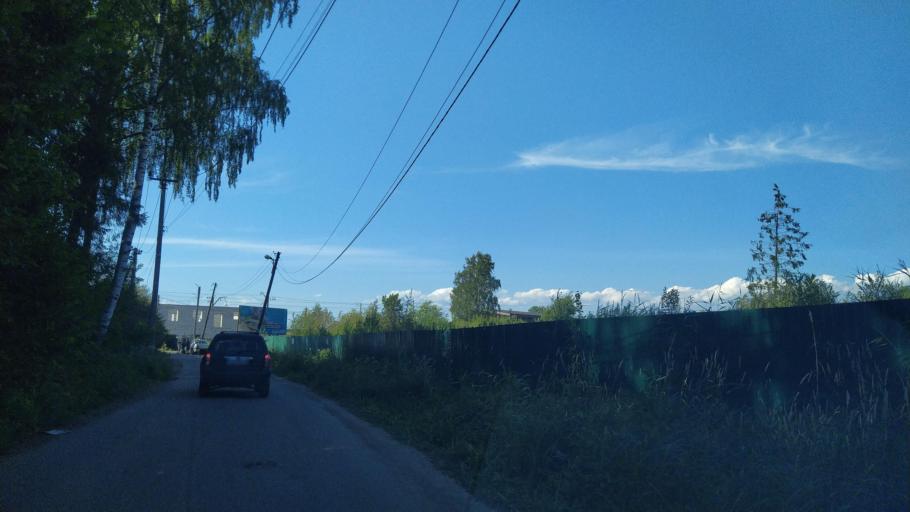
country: RU
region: Leningrad
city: Toksovo
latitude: 60.1732
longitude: 30.5287
